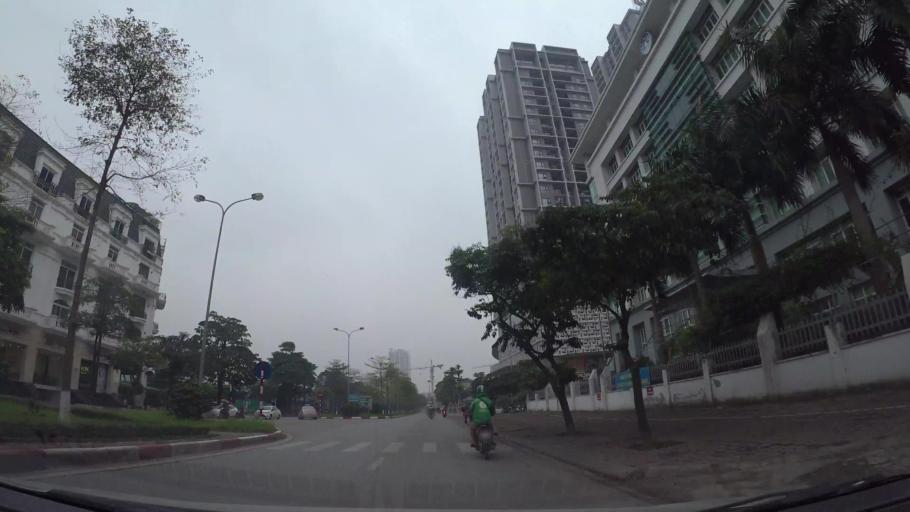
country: VN
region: Ha Noi
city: Cau Giay
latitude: 21.0278
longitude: 105.7852
